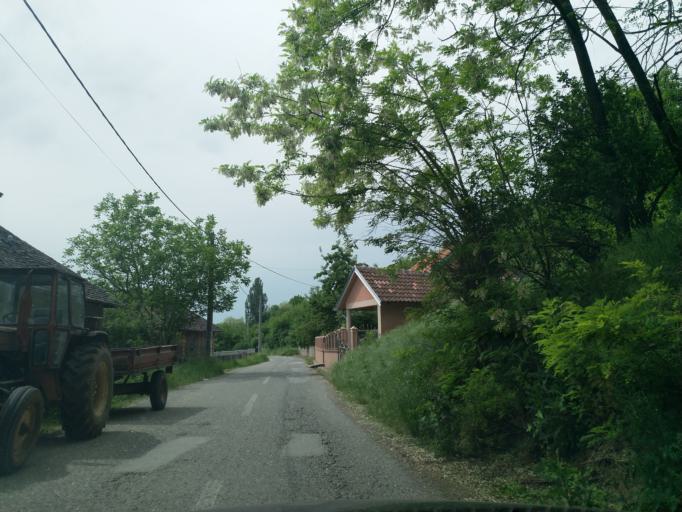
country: RS
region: Central Serbia
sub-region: Pomoravski Okrug
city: Paracin
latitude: 43.8632
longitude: 21.5858
